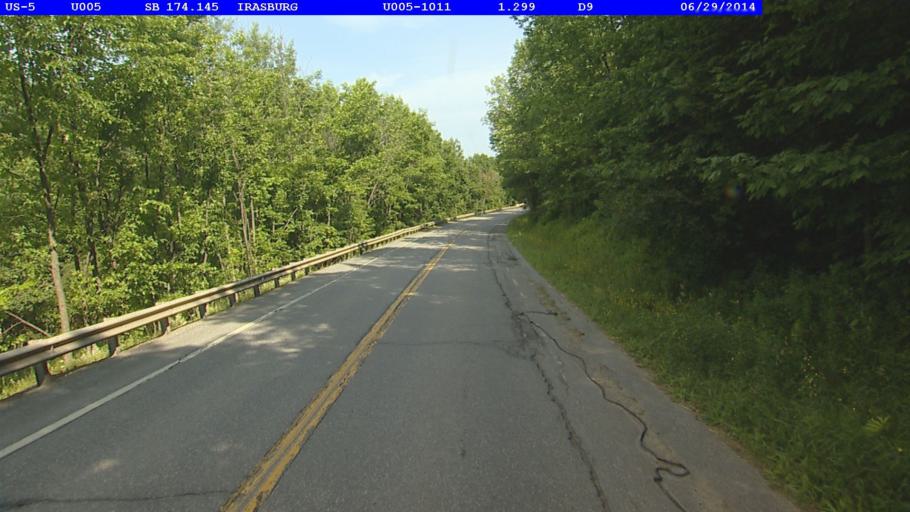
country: US
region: Vermont
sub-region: Orleans County
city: Newport
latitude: 44.8223
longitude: -72.2277
